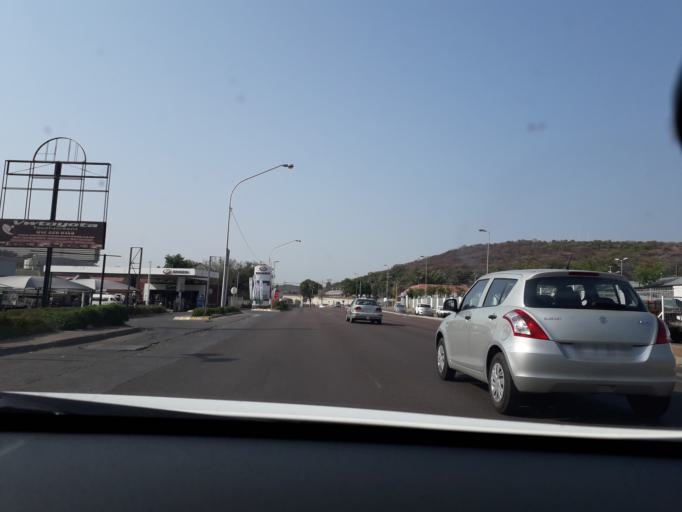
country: ZA
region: Gauteng
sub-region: City of Tshwane Metropolitan Municipality
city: Pretoria
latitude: -25.7592
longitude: 28.1918
